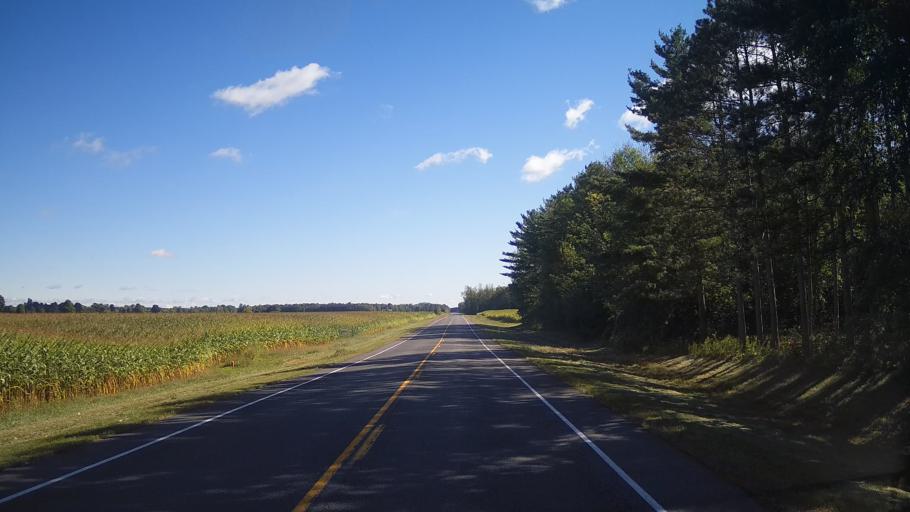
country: CA
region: Ontario
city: Prescott
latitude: 44.9054
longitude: -75.4407
